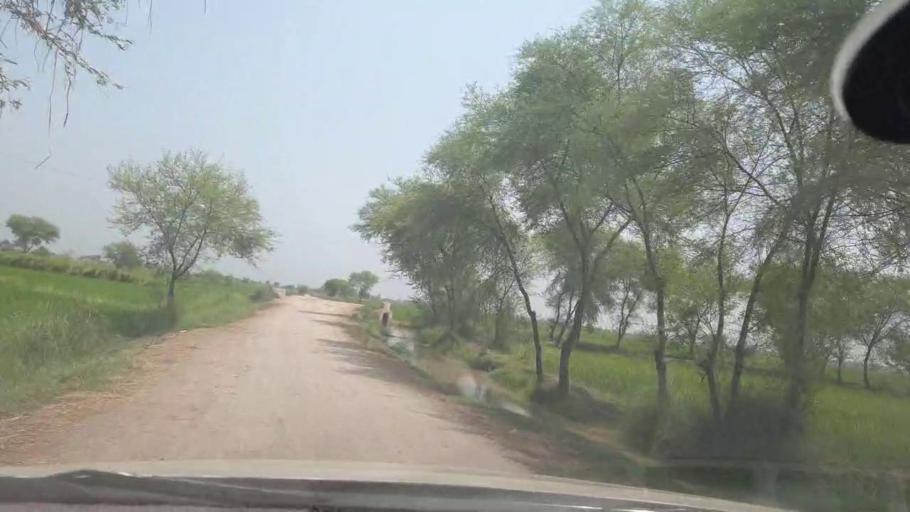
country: PK
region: Sindh
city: Jacobabad
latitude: 28.1728
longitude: 68.3881
